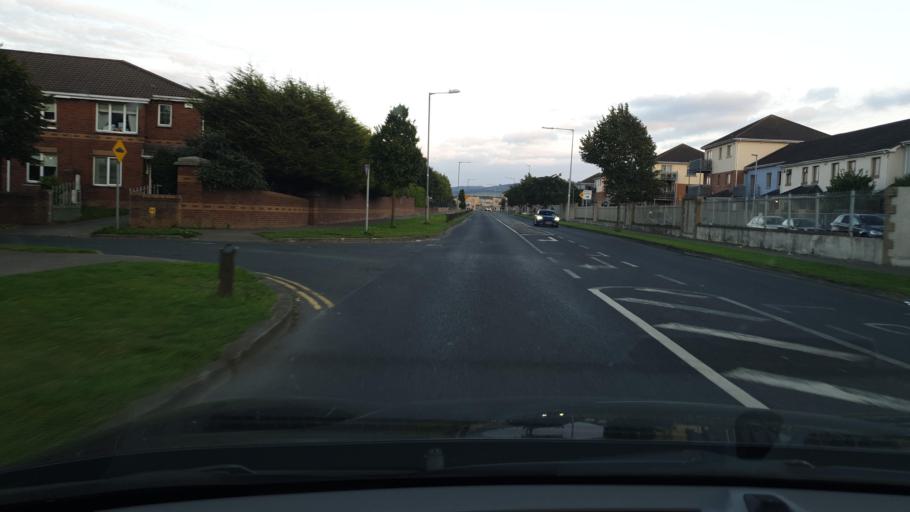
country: IE
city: Jobstown
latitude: 53.2849
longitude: -6.4060
